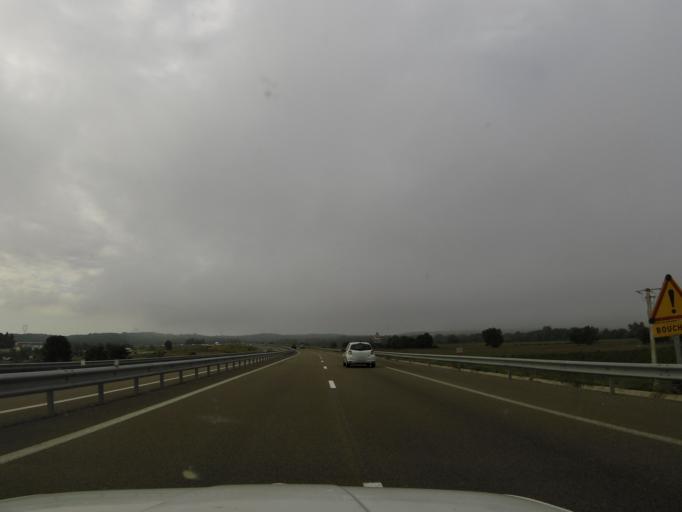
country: FR
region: Languedoc-Roussillon
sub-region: Departement du Gard
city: La Calmette
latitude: 43.9283
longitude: 4.2546
